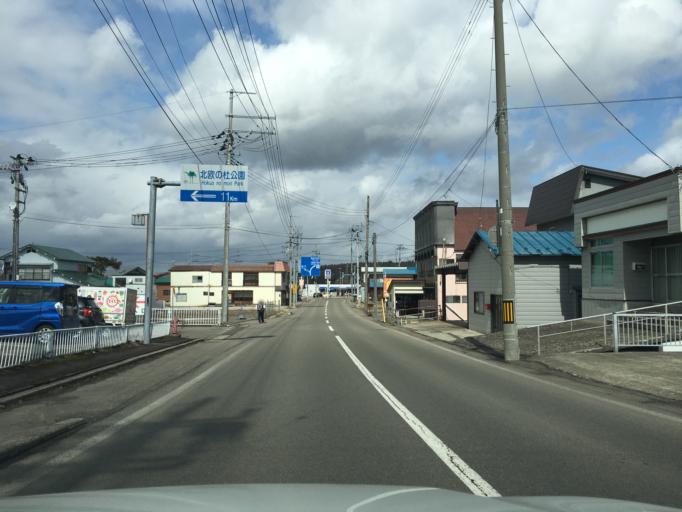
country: JP
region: Akita
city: Takanosu
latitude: 40.1221
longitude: 140.3673
